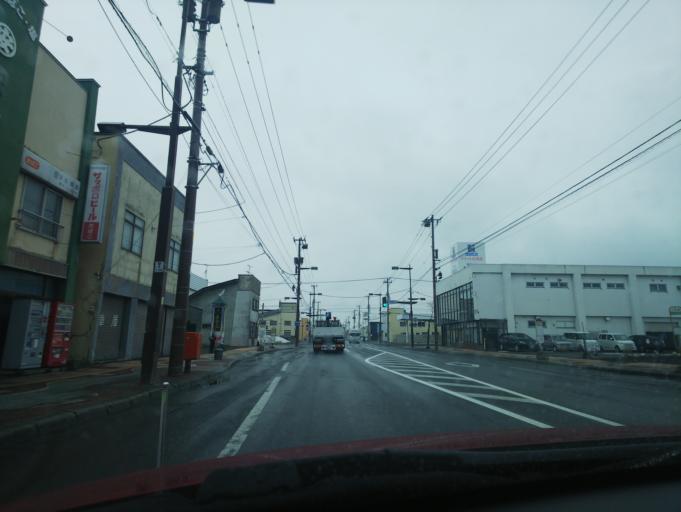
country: JP
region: Hokkaido
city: Nayoro
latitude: 44.1801
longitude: 142.3910
